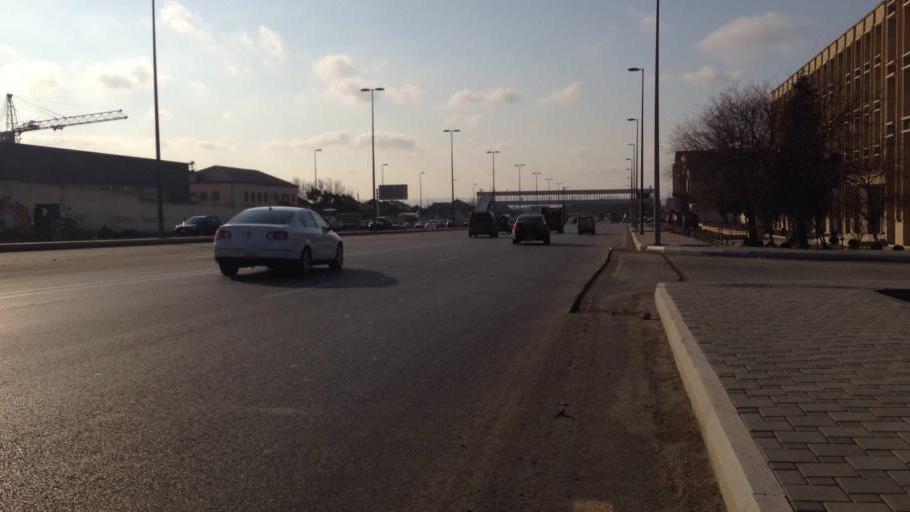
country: AZ
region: Baki
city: Balakhani
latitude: 40.4260
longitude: 49.9104
